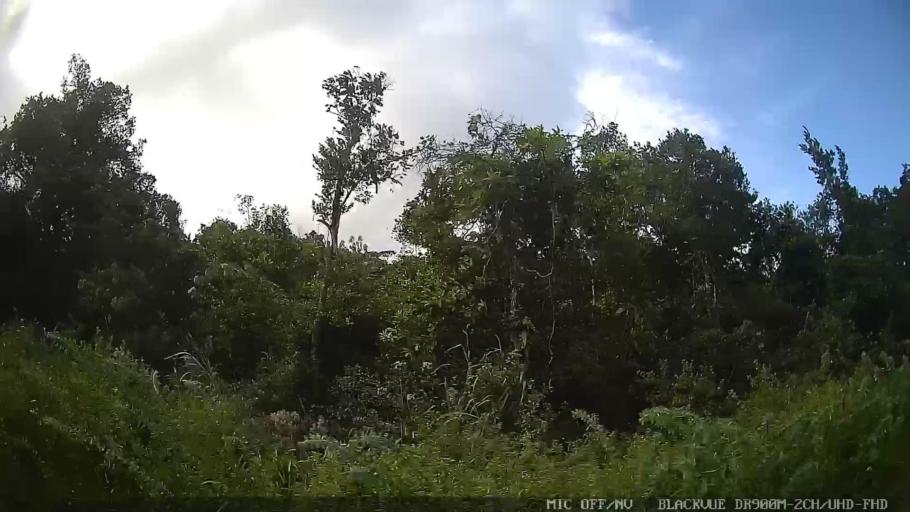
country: BR
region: Sao Paulo
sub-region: Itanhaem
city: Itanhaem
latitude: -24.2189
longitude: -46.9120
